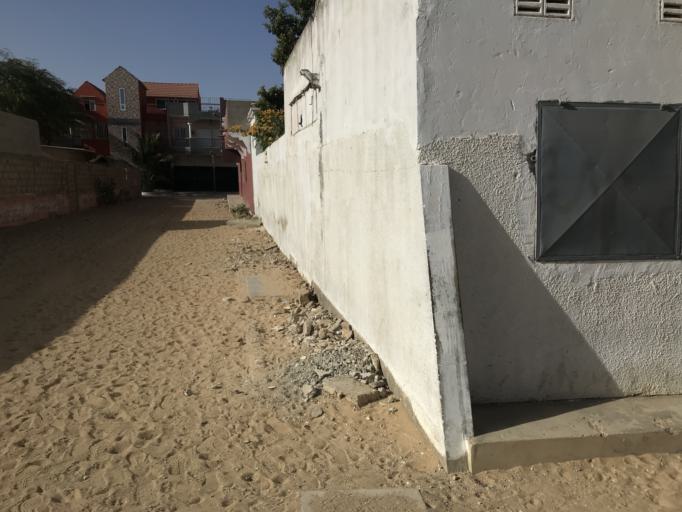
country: SN
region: Saint-Louis
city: Saint-Louis
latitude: 16.0378
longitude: -16.4464
